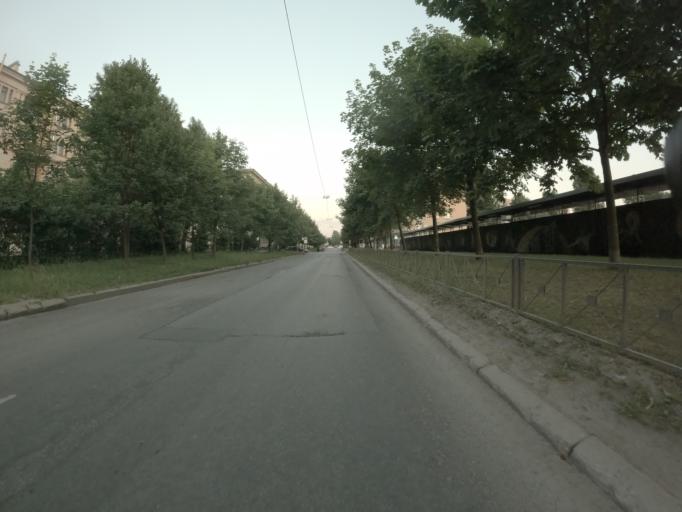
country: RU
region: St.-Petersburg
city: Centralniy
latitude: 59.9296
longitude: 30.4057
